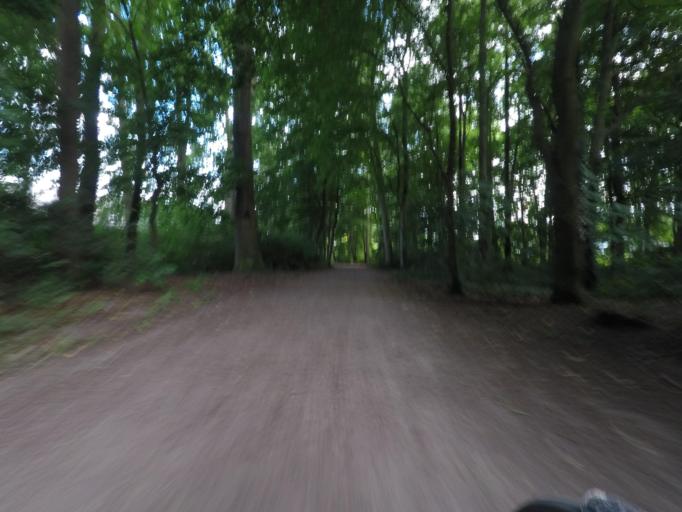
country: DE
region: Hamburg
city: Sasel
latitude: 53.6434
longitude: 10.1128
